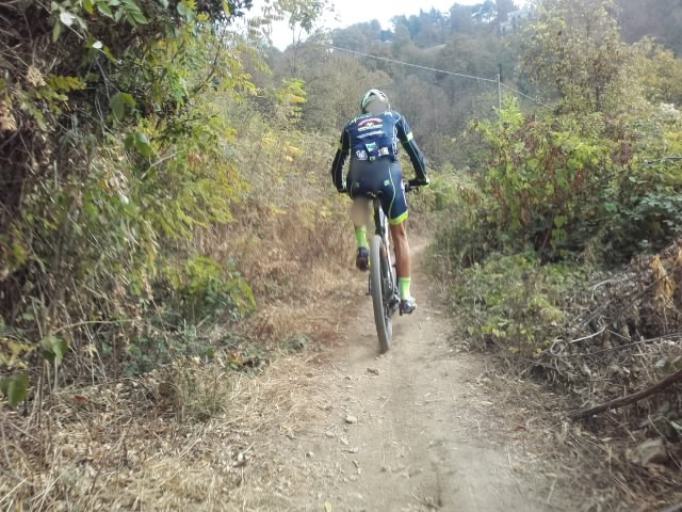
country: IT
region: Piedmont
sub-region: Provincia di Torino
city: San Mauro Torinese
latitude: 45.0759
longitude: 7.7695
